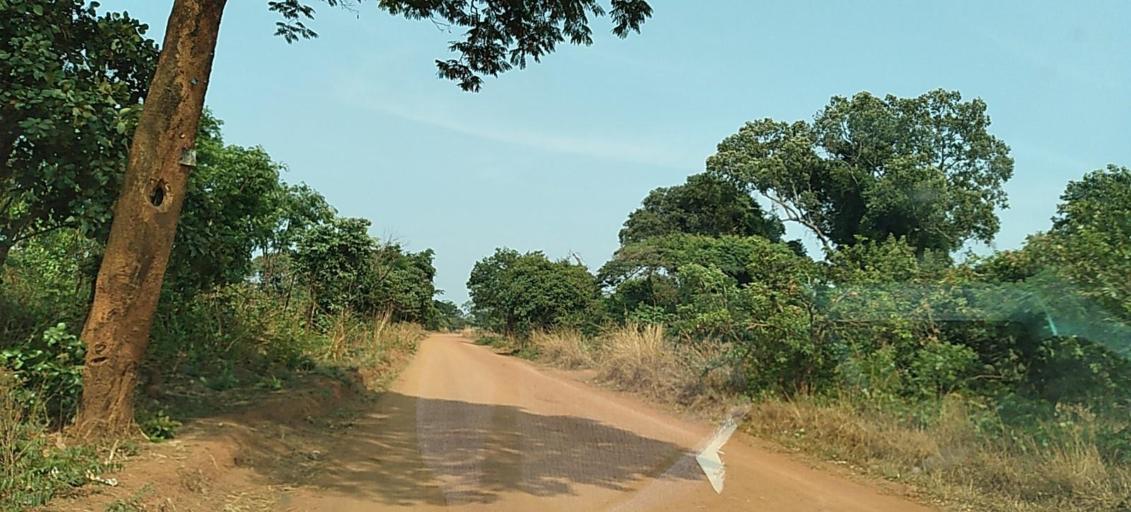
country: ZM
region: Copperbelt
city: Chililabombwe
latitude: -12.3406
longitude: 27.6902
